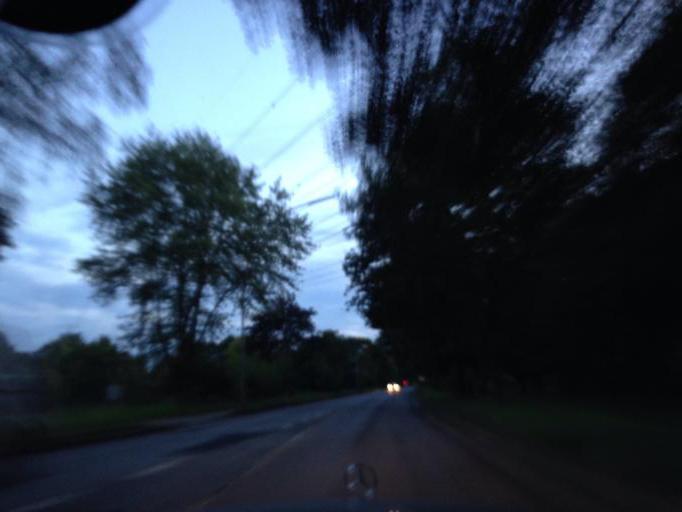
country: DE
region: Schleswig-Holstein
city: Stapelfeld
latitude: 53.6346
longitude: 10.1878
